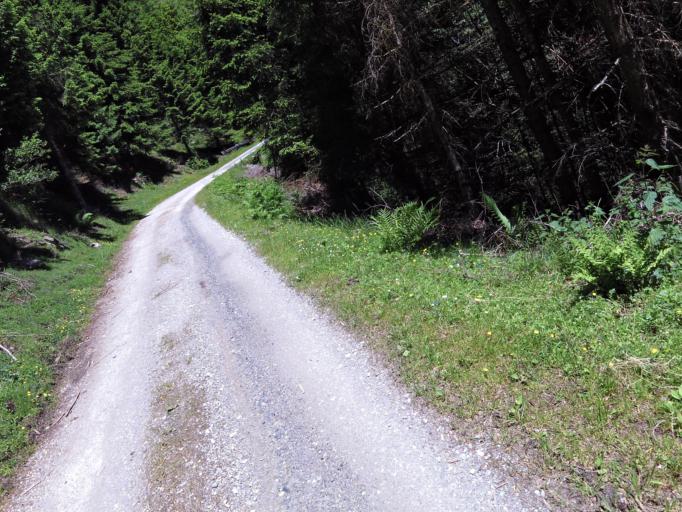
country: AT
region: Tyrol
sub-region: Politischer Bezirk Innsbruck Land
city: Neustift im Stubaital
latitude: 47.1118
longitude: 11.2898
